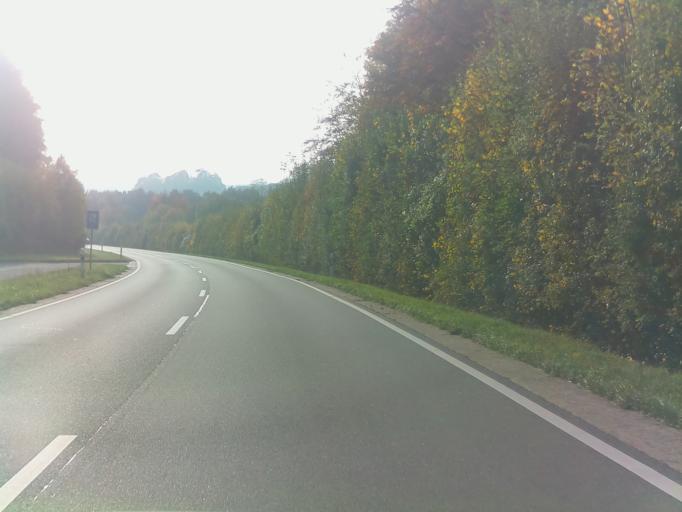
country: DE
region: Baden-Wuerttemberg
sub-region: Karlsruhe Region
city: Limbach
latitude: 49.4096
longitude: 9.2379
